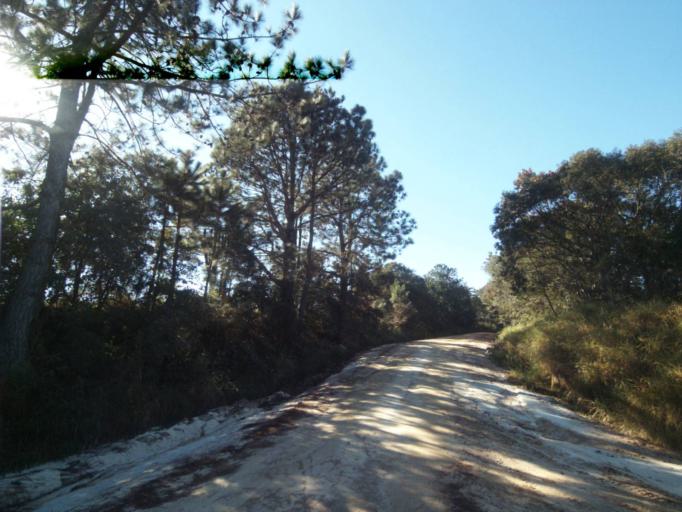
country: BR
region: Parana
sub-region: Tibagi
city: Tibagi
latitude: -24.5338
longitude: -50.3760
